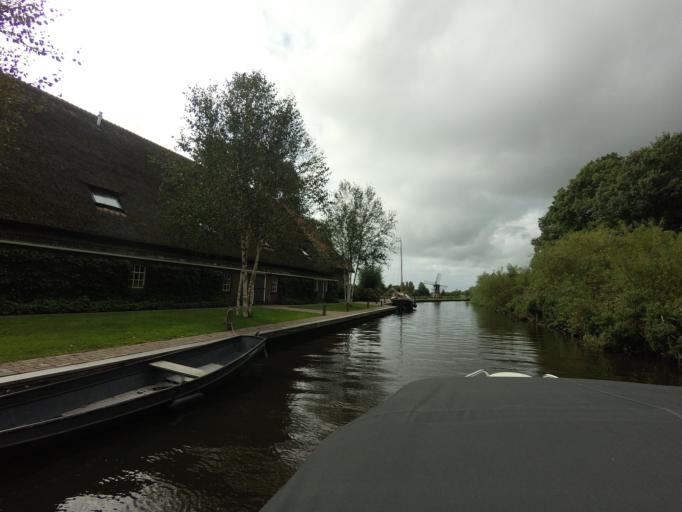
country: NL
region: Friesland
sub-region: Gemeente Boarnsterhim
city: Warten
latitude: 53.1388
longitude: 5.9123
